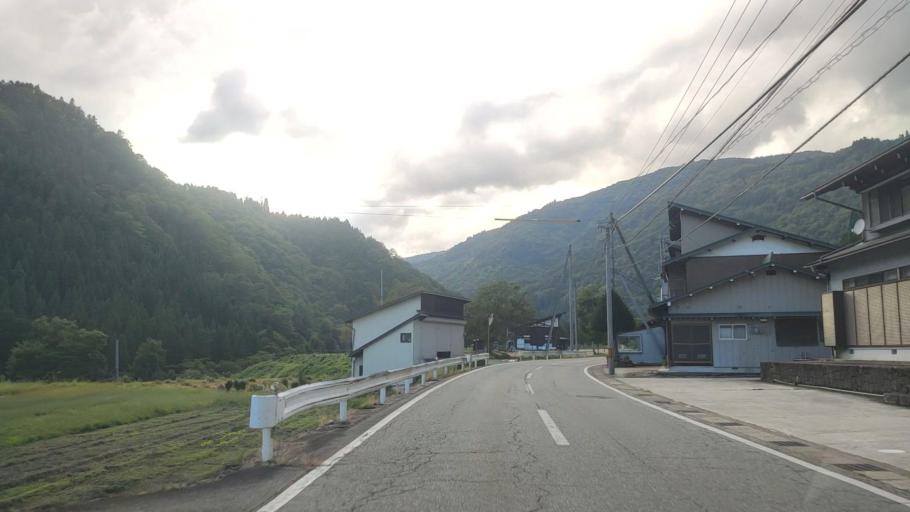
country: JP
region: Gifu
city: Takayama
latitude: 36.3047
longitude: 137.0976
